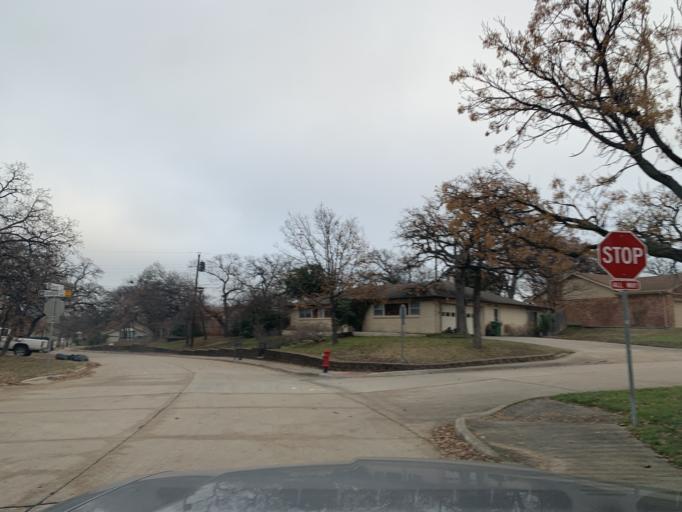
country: US
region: Texas
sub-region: Tarrant County
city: Bedford
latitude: 32.8381
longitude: -97.1568
